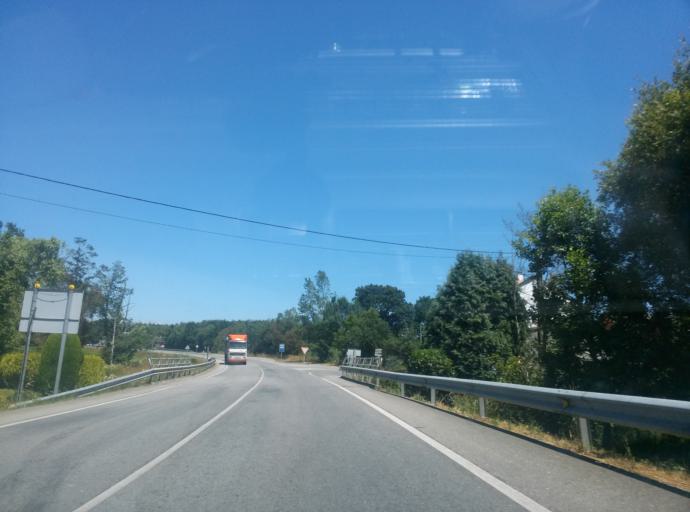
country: ES
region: Galicia
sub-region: Provincia de Lugo
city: Castro de Rei
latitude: 43.1829
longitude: -7.4743
